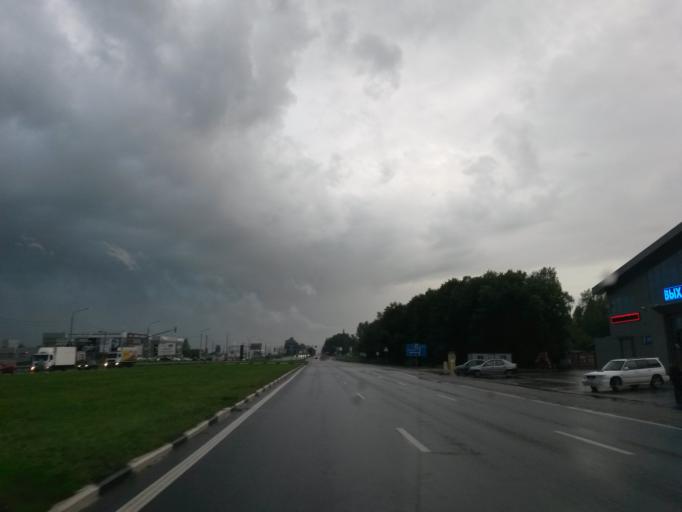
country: RU
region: Jaroslavl
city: Yaroslavl
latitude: 57.5644
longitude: 39.8286
